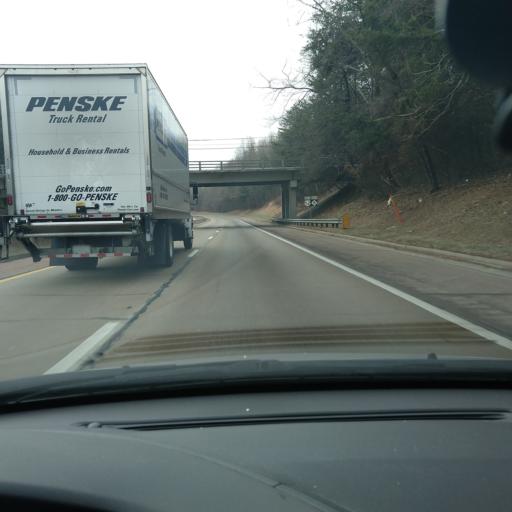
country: US
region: North Carolina
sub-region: Forsyth County
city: Winston-Salem
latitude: 36.0422
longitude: -80.2391
